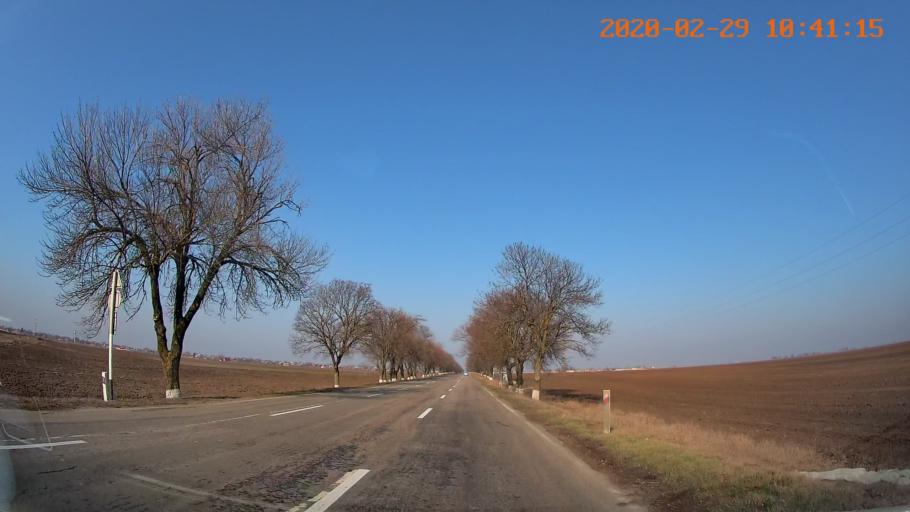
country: MD
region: Telenesti
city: Grigoriopol
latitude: 47.0406
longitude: 29.4279
